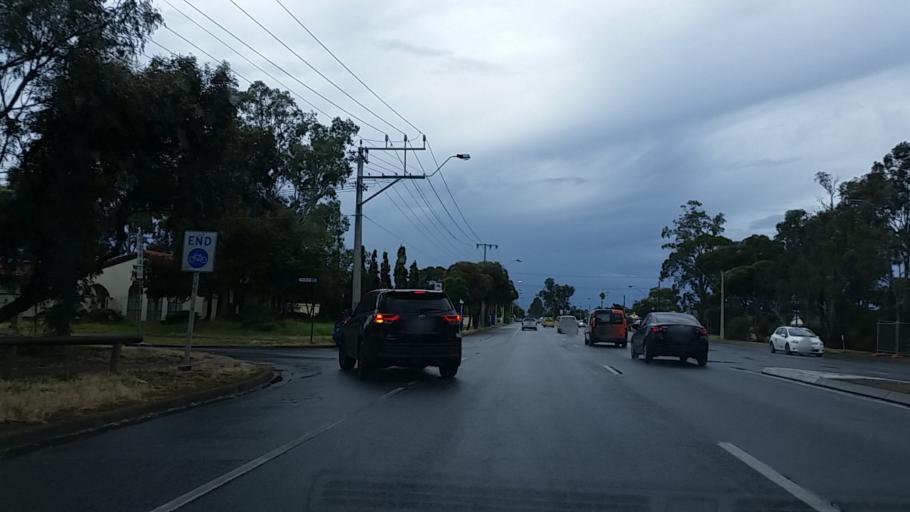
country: AU
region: South Australia
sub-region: Salisbury
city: Salisbury
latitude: -34.7965
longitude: 138.6108
